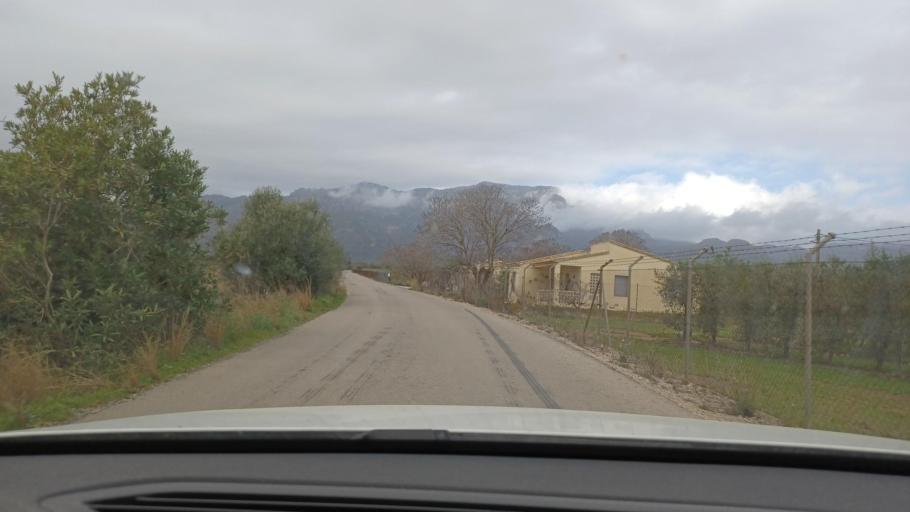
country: ES
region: Catalonia
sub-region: Provincia de Tarragona
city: Tortosa
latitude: 40.7954
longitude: 0.4441
